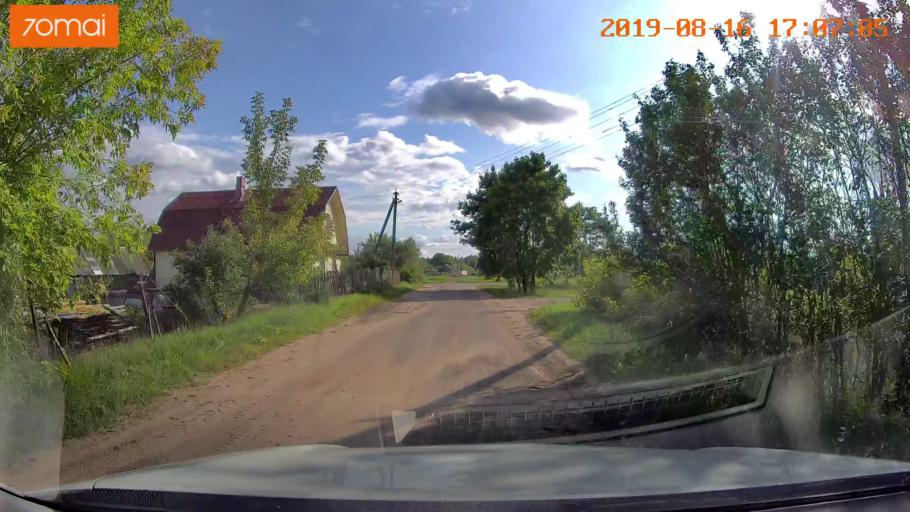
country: BY
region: Mogilev
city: Hlusha
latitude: 53.2212
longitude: 28.9271
